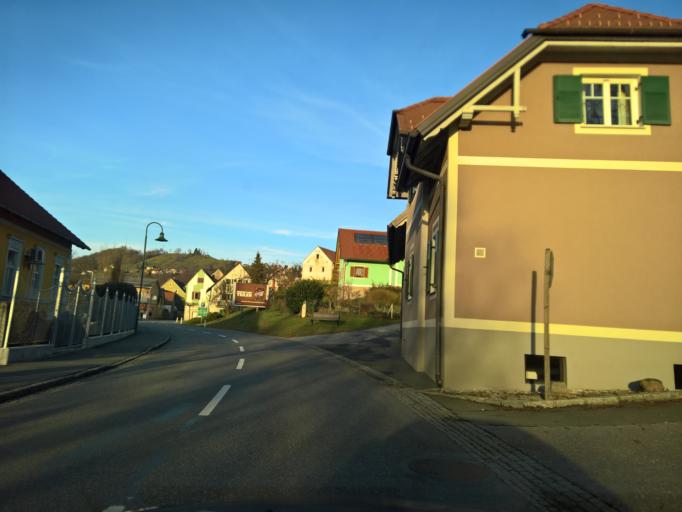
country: AT
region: Styria
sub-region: Politischer Bezirk Leibnitz
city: Grossklein
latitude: 46.7361
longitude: 15.4414
